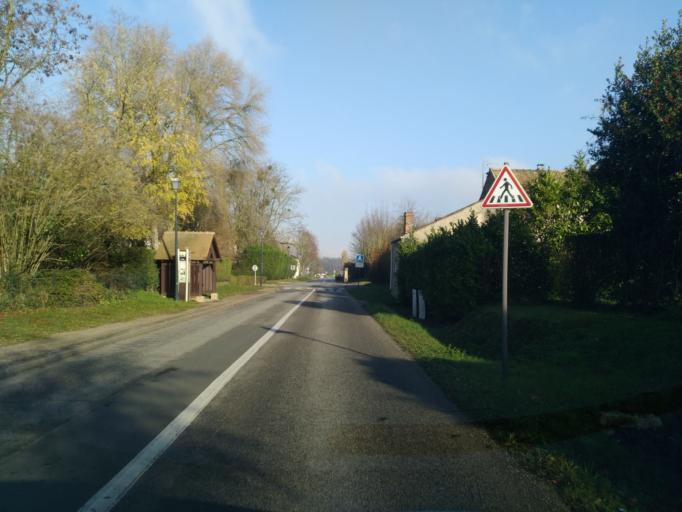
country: FR
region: Ile-de-France
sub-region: Departement des Yvelines
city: Feucherolles
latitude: 48.8816
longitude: 1.9813
